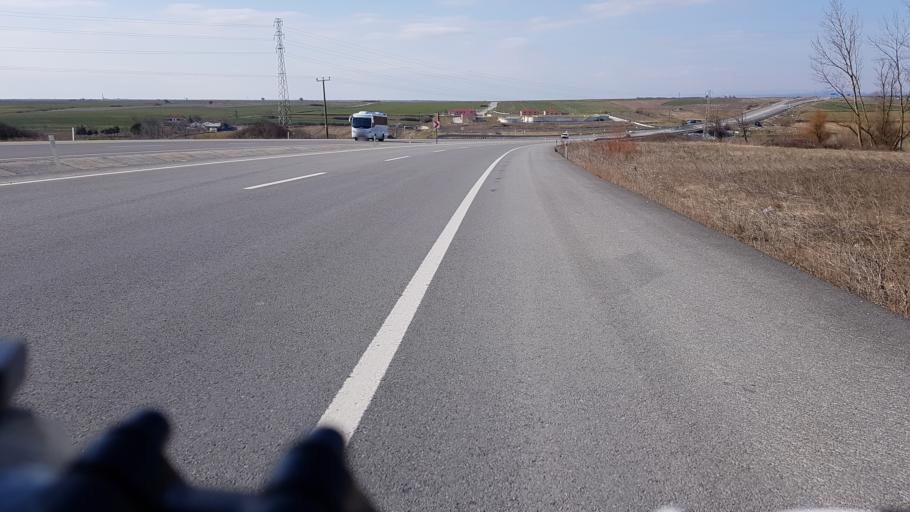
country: TR
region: Tekirdag
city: Saray
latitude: 41.4221
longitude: 27.9156
